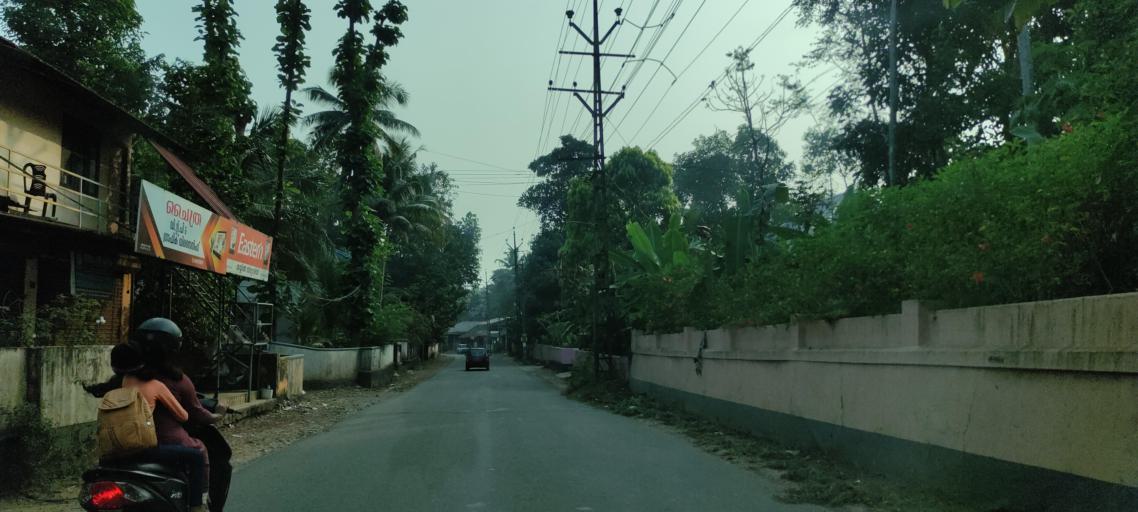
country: IN
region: Kerala
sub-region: Kottayam
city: Vaikam
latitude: 9.7171
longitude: 76.4758
